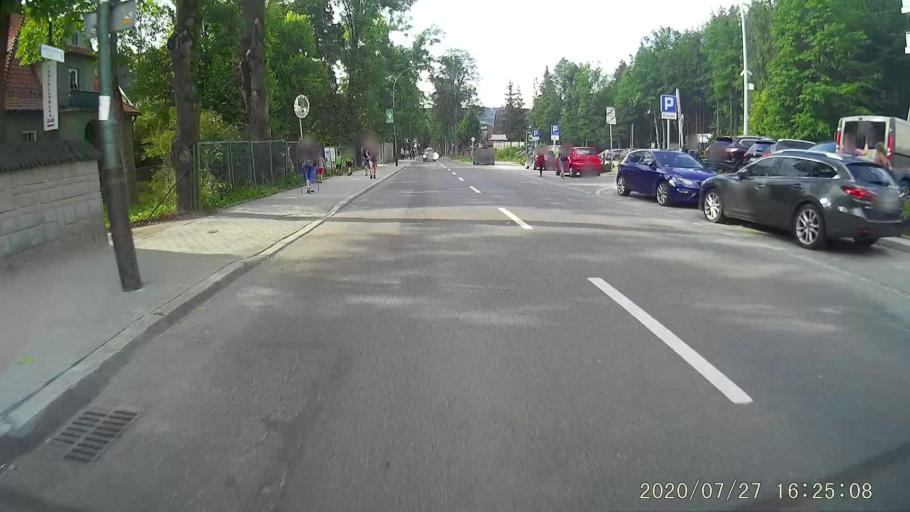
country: PL
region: Lesser Poland Voivodeship
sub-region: Powiat tatrzanski
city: Zakopane
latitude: 49.2958
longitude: 19.9639
